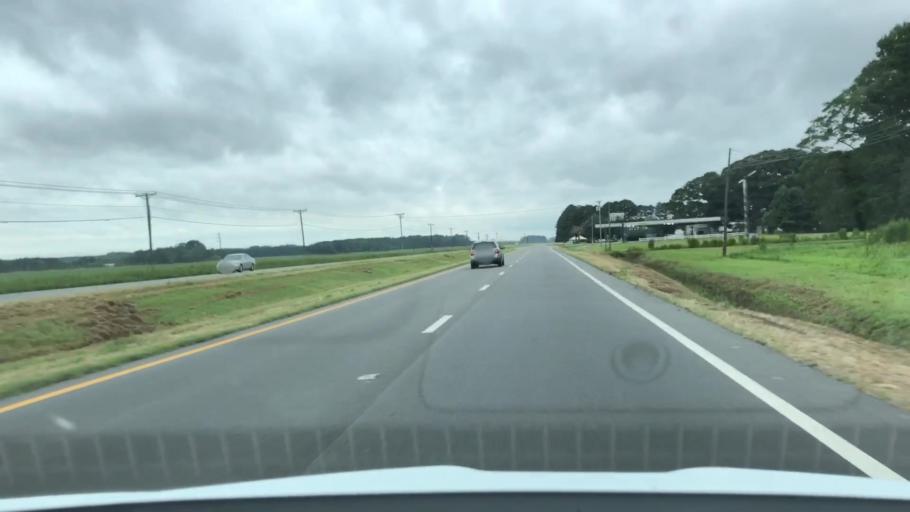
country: US
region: North Carolina
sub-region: Lenoir County
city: La Grange
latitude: 35.2601
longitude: -77.7049
